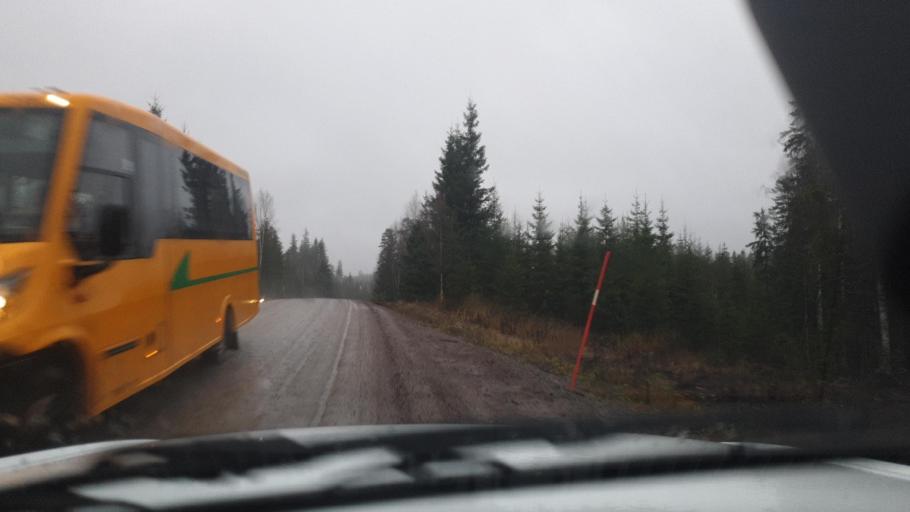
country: SE
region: Vaermland
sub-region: Arvika Kommun
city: Arvika
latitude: 59.9459
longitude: 12.6616
